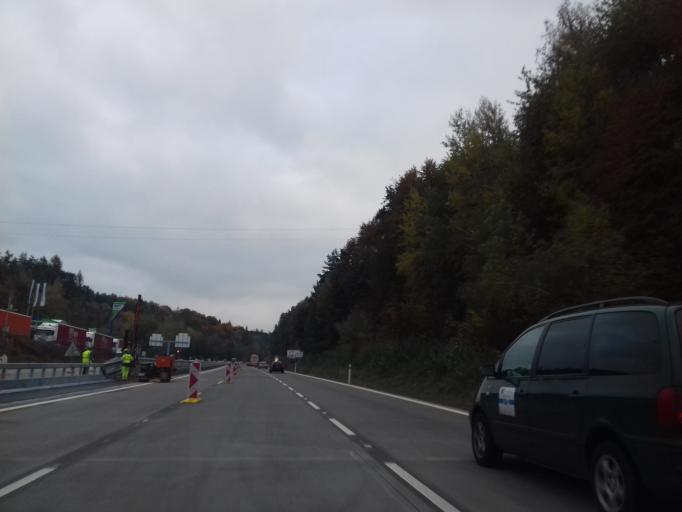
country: CZ
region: Central Bohemia
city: Ondrejov
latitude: 49.8617
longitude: 14.7893
